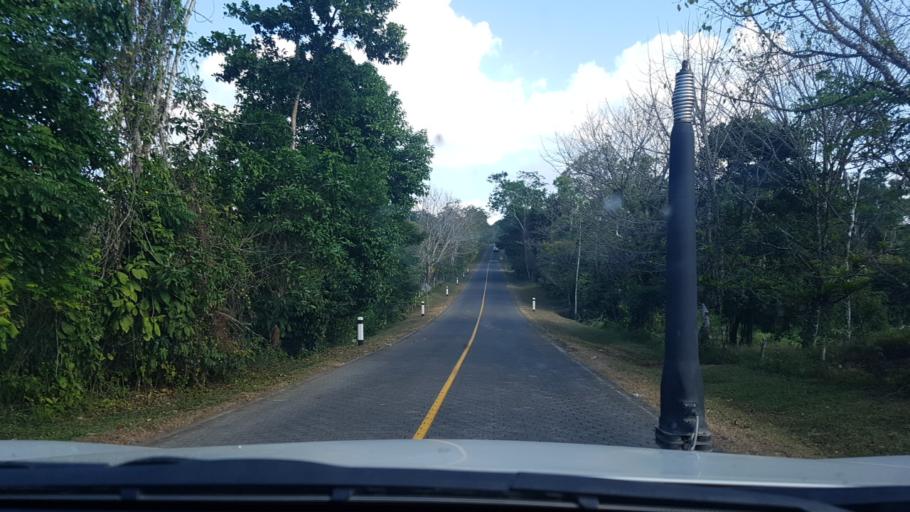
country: NI
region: Atlantico Sur
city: Nueva Guinea
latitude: 11.6958
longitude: -84.4068
